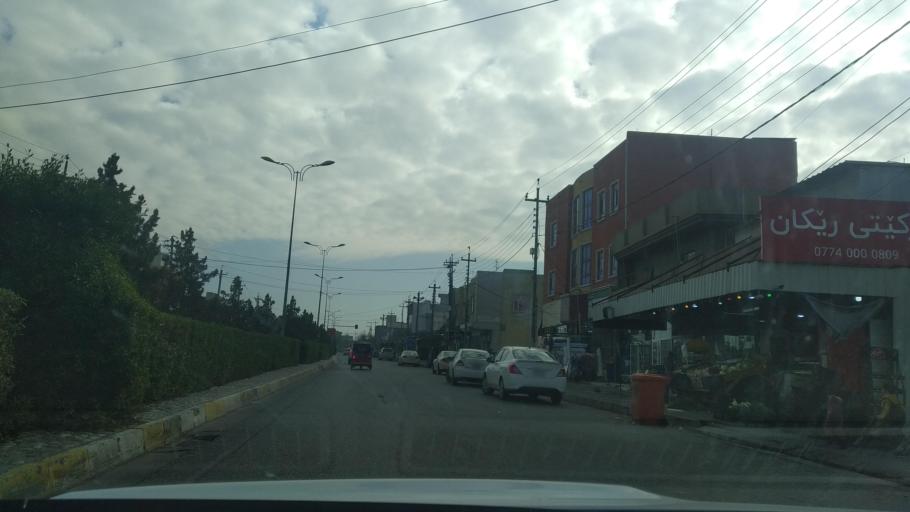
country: IQ
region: Arbil
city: Erbil
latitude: 36.1770
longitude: 44.0301
